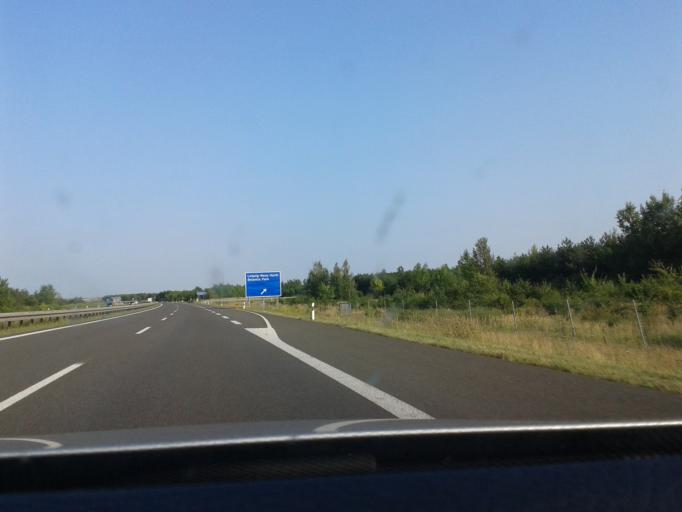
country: DE
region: Saxony
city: Zwenkau
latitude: 51.2533
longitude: 12.3026
